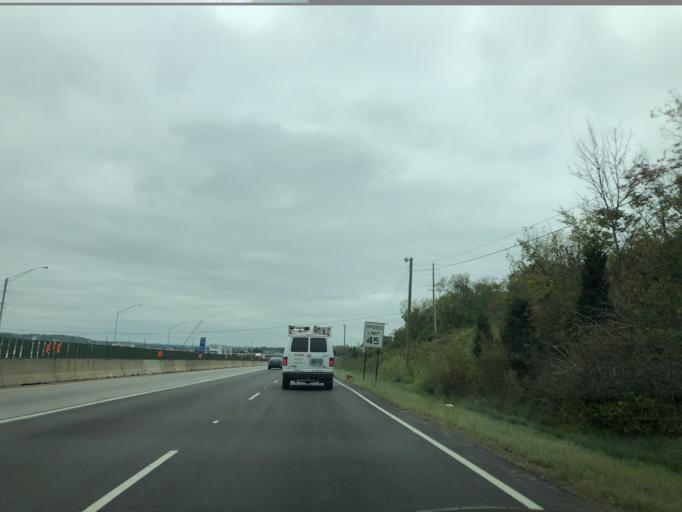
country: US
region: Ohio
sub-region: Hamilton County
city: Glendale
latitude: 39.2595
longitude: -84.4414
